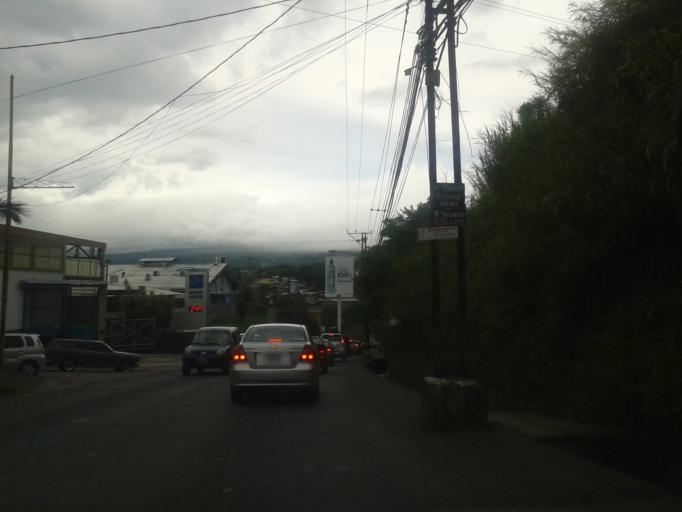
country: CR
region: San Jose
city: San Juan
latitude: 9.9644
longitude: -84.0862
